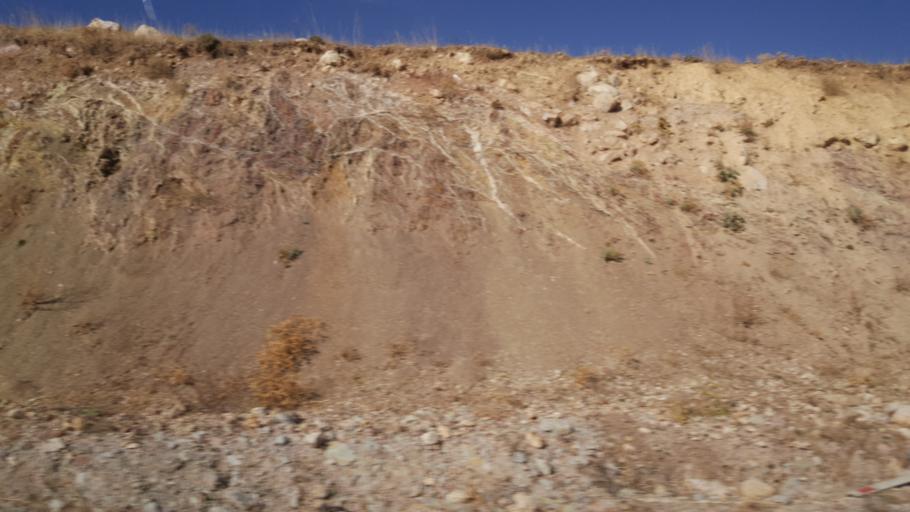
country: TR
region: Ankara
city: Ikizce
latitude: 39.5446
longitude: 32.6473
